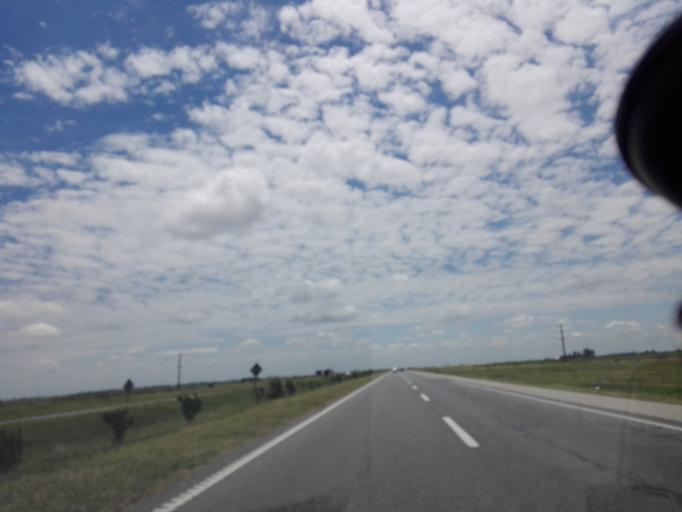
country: AR
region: Cordoba
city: James Craik
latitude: -32.0826
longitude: -63.4826
